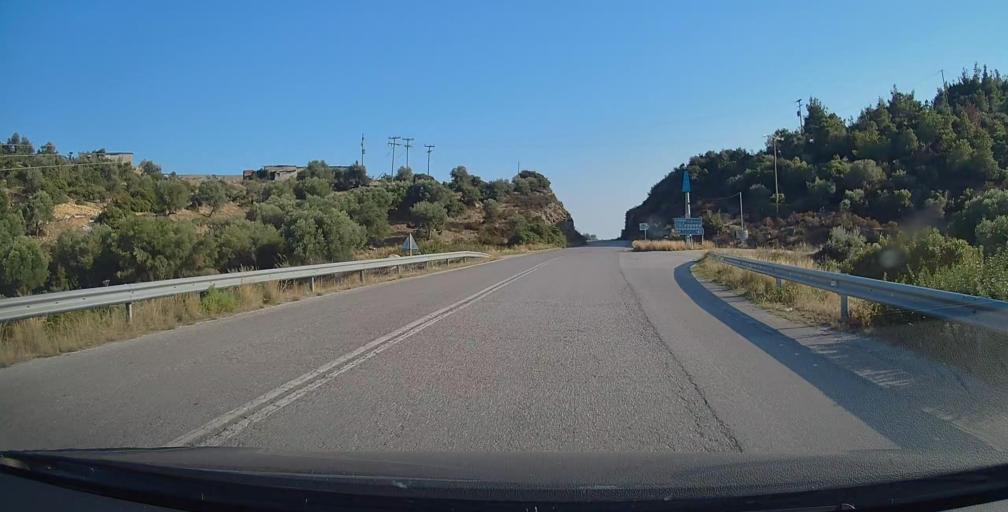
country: GR
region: Central Macedonia
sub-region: Nomos Chalkidikis
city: Sykia
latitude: 40.0009
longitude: 23.8883
